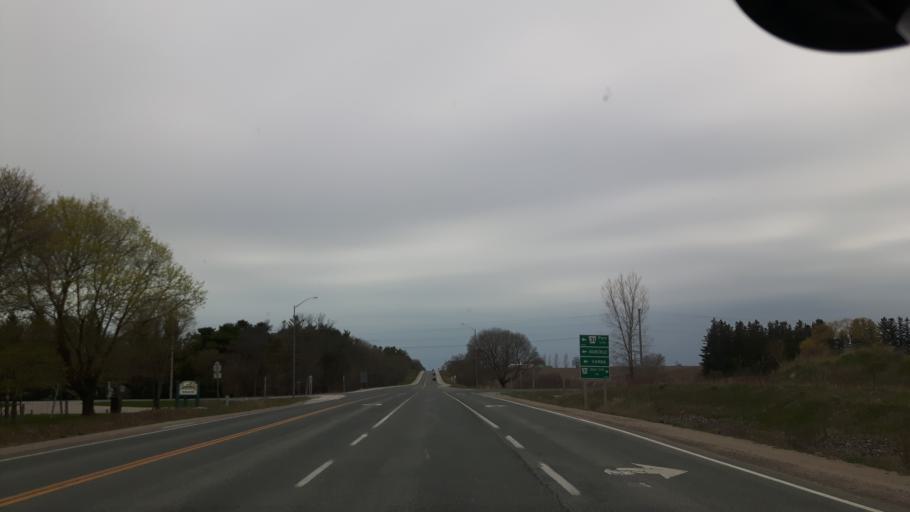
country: CA
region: Ontario
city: Goderich
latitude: 43.6460
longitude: -81.6006
